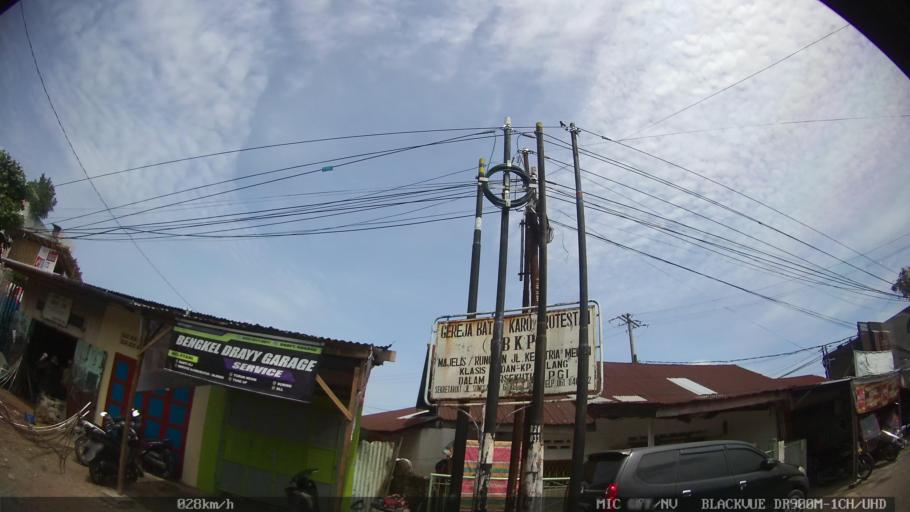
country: ID
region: North Sumatra
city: Sunggal
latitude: 3.5819
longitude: 98.6403
